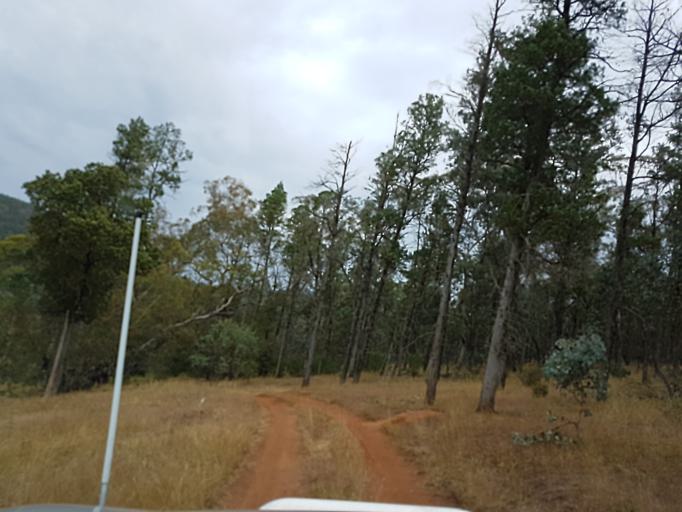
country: AU
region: New South Wales
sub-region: Snowy River
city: Jindabyne
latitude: -36.9342
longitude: 148.4002
